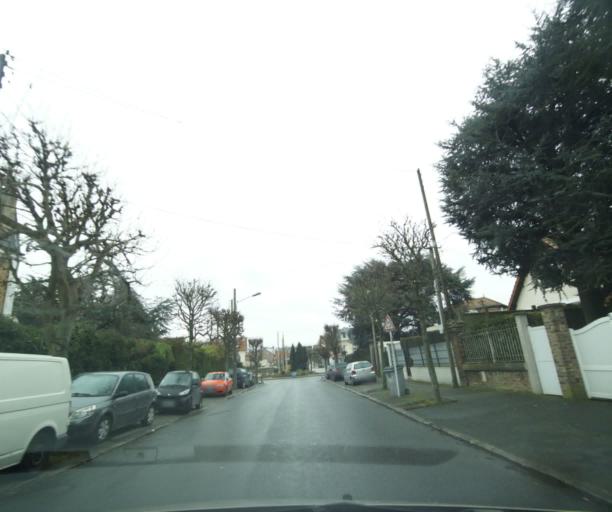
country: FR
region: Ile-de-France
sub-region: Departement du Val-de-Marne
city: Ablon-sur-Seine
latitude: 48.7327
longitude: 2.4237
